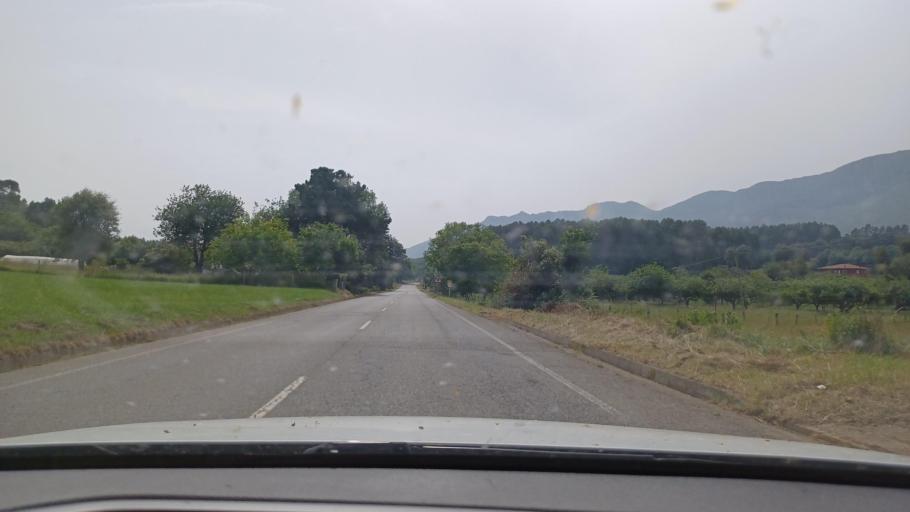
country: ES
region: Asturias
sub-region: Province of Asturias
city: Ribadesella
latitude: 43.4532
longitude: -5.0312
